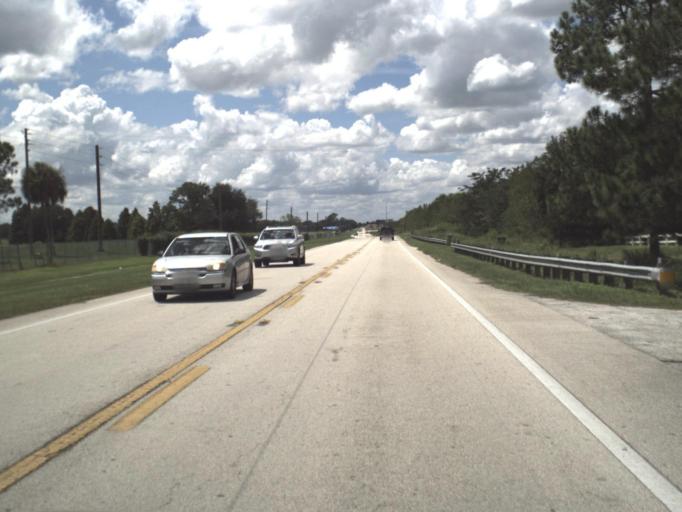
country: US
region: Florida
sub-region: Polk County
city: Dundee
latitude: 28.0188
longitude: -81.6445
